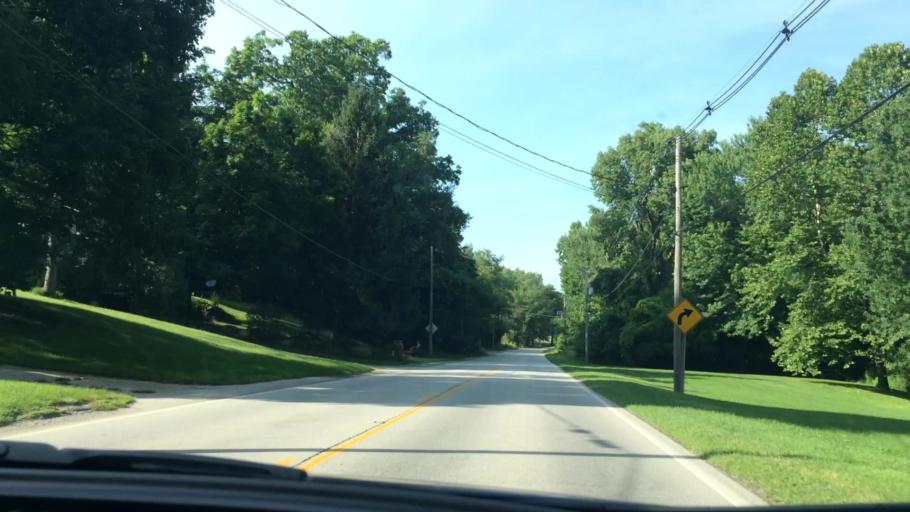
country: US
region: Indiana
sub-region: Tippecanoe County
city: West Lafayette
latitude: 40.4550
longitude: -86.8943
